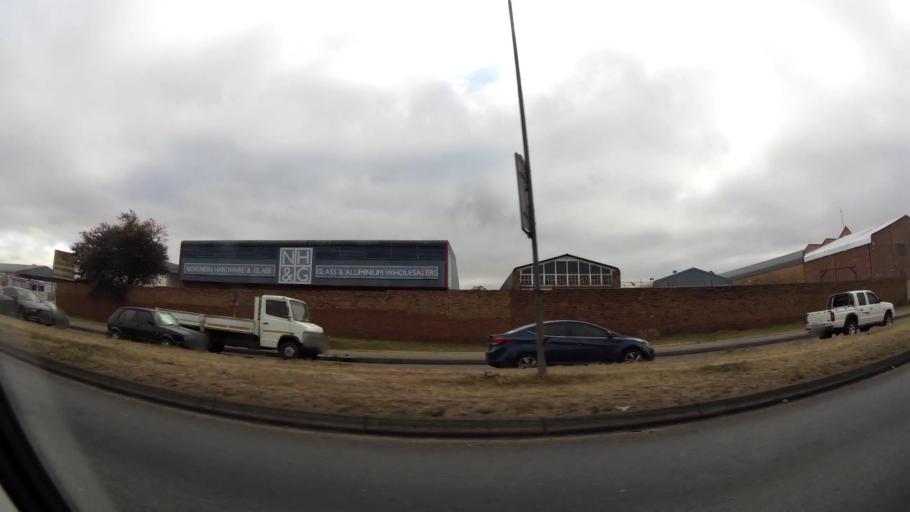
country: ZA
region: Limpopo
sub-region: Capricorn District Municipality
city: Polokwane
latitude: -23.8916
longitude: 29.4350
